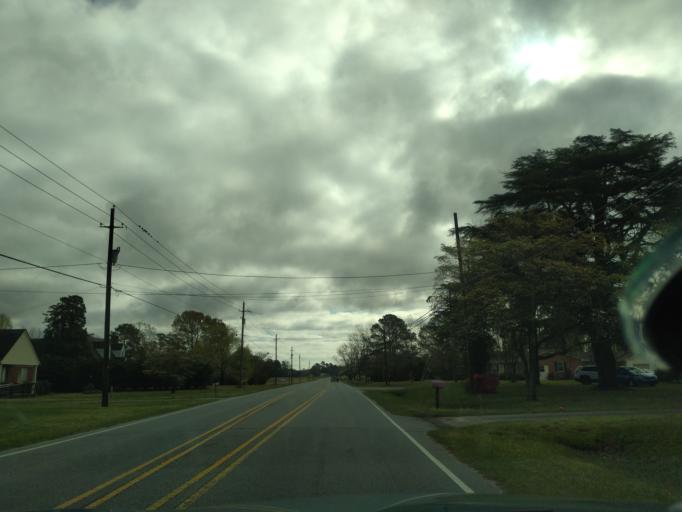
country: US
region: North Carolina
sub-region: Chowan County
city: Edenton
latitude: 36.0570
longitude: -76.6532
